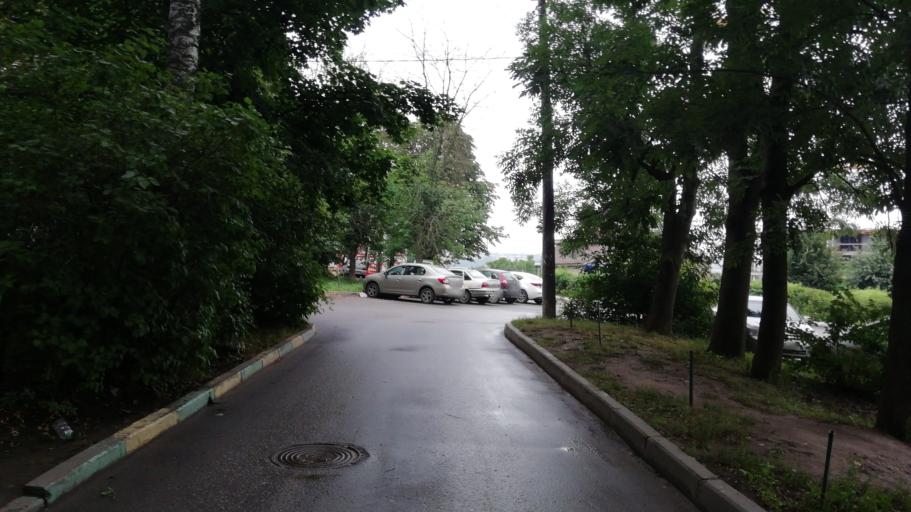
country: RU
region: Tula
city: Mendeleyevskiy
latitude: 54.1672
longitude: 37.5674
